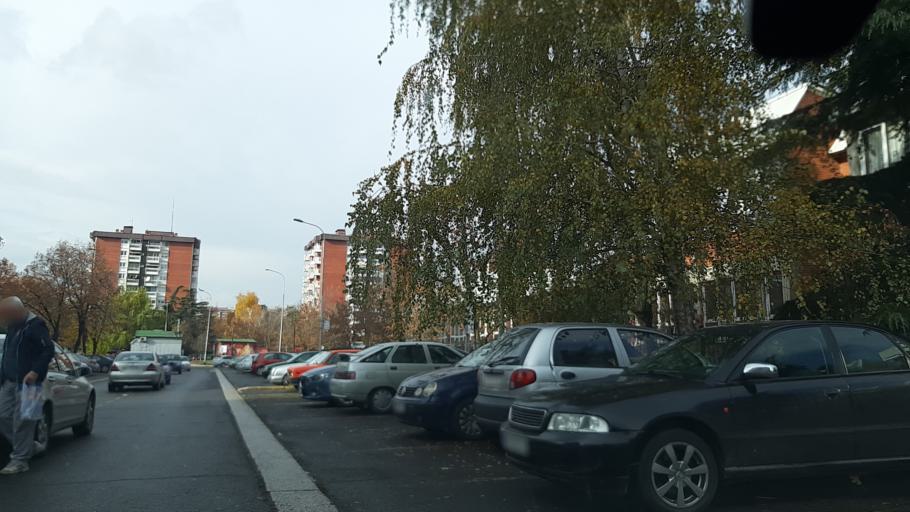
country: MK
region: Kisela Voda
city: Usje
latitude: 41.9887
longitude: 21.4648
